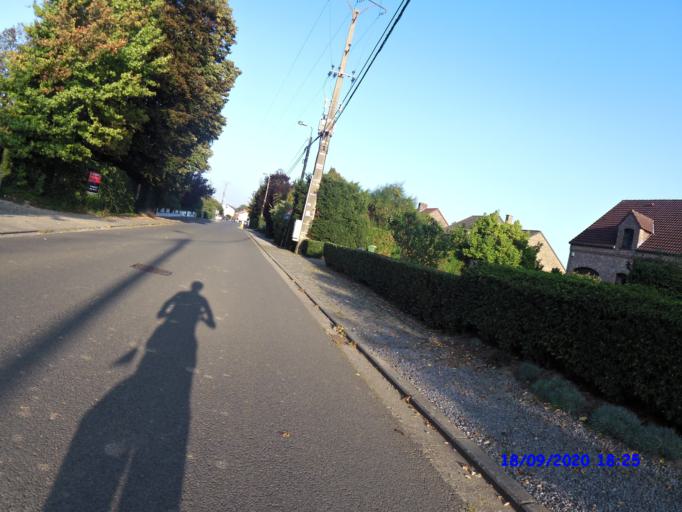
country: BE
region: Wallonia
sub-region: Province de Liege
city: Berloz
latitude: 50.6961
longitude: 5.2322
